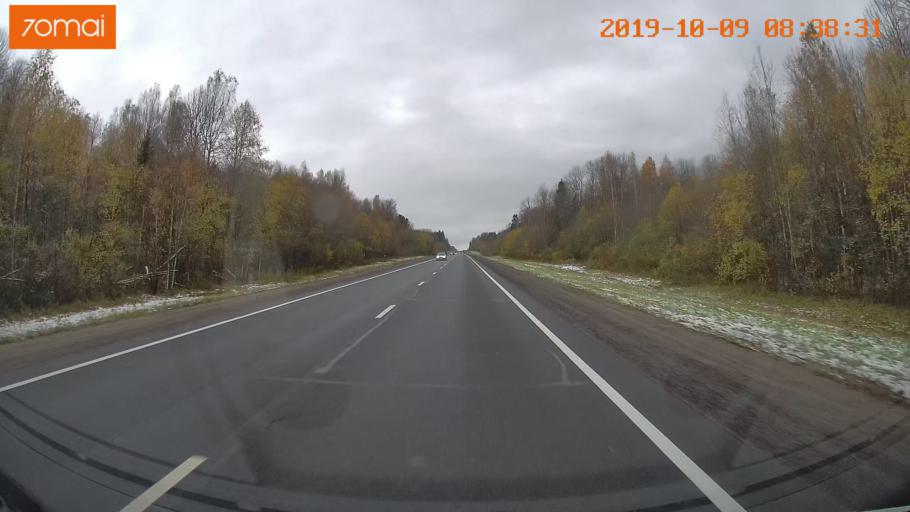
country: RU
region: Vologda
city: Gryazovets
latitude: 58.9577
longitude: 40.1647
